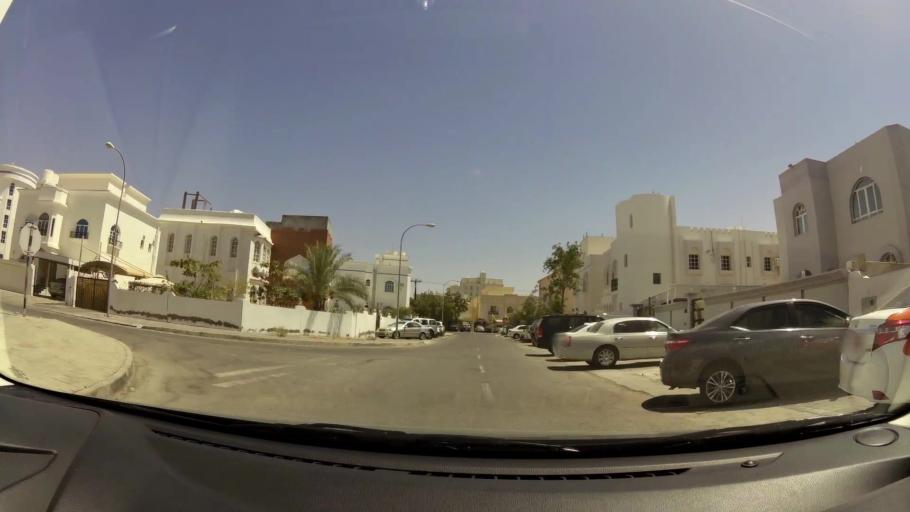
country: OM
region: Muhafazat Masqat
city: Bawshar
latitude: 23.5957
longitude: 58.3717
